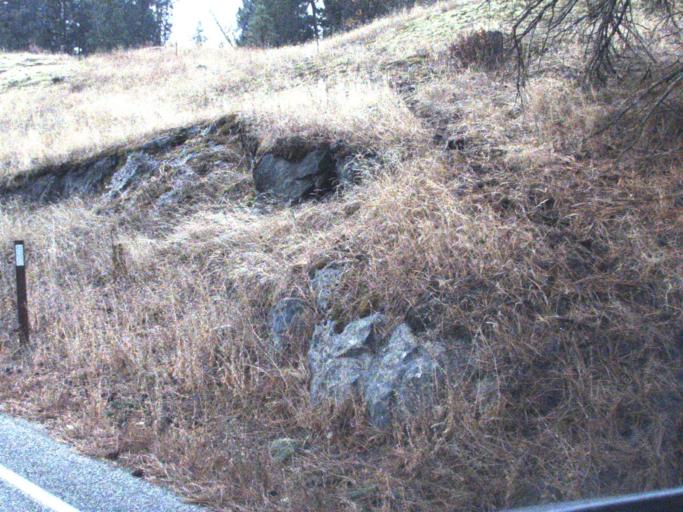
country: CA
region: British Columbia
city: Grand Forks
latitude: 48.8659
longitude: -118.2065
